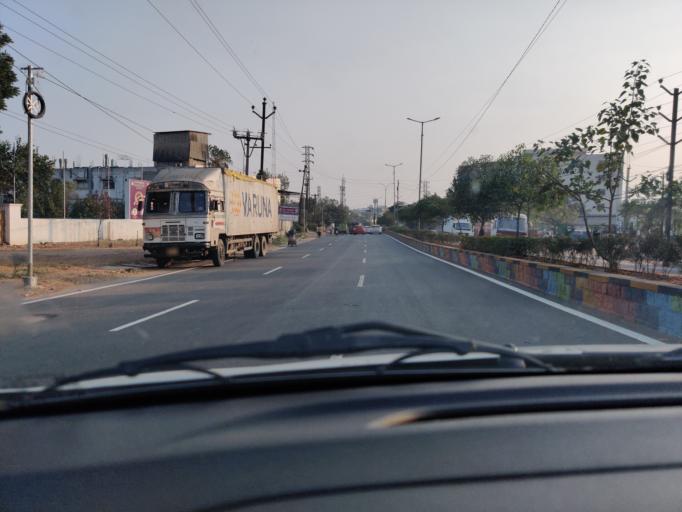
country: IN
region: Telangana
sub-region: Rangareddi
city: Uppal Kalan
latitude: 17.4353
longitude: 78.5547
